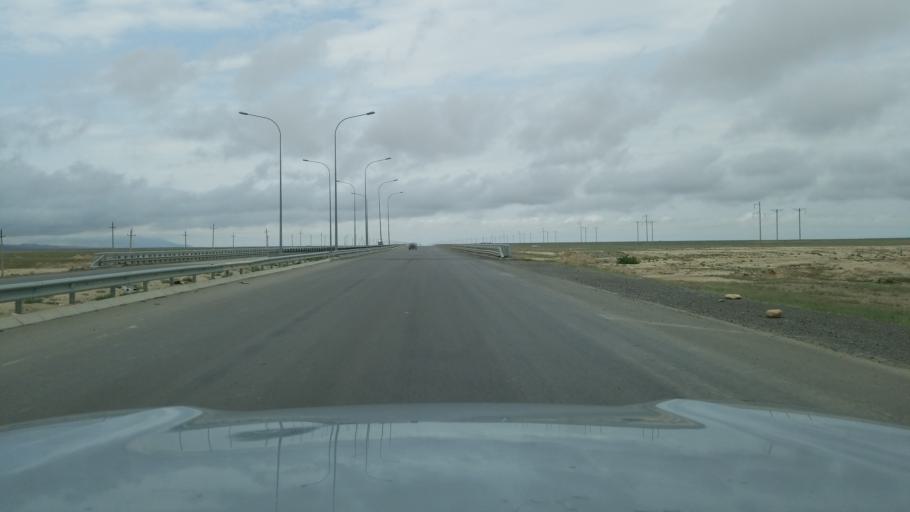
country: TM
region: Balkan
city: Gazanjyk
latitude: 39.1264
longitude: 55.8974
